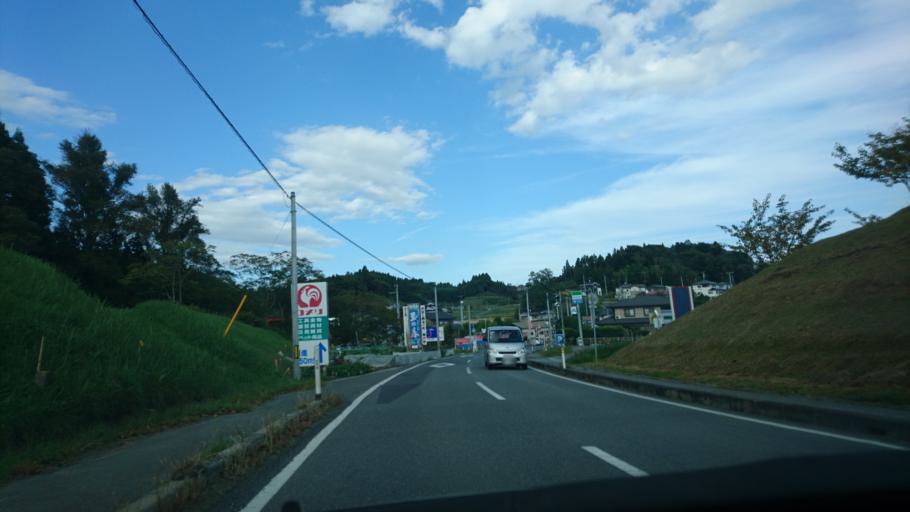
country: JP
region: Iwate
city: Ichinoseki
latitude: 38.8688
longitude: 141.3513
